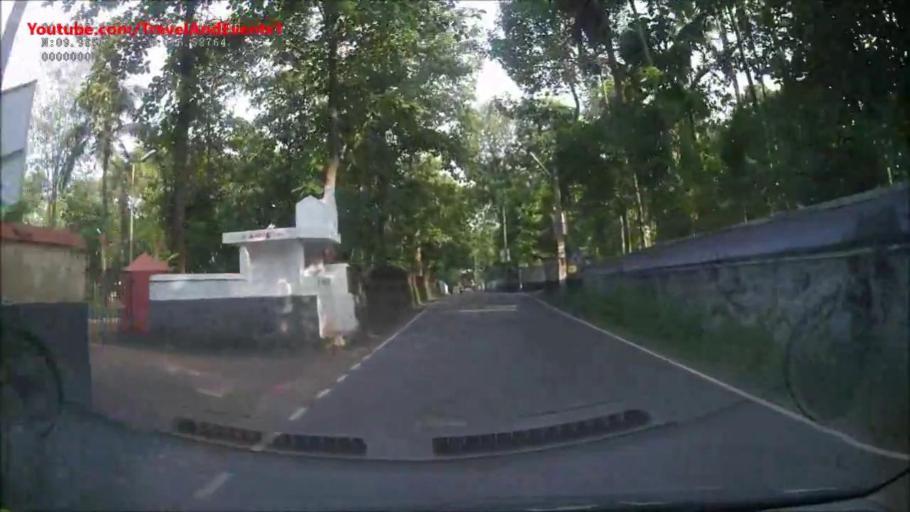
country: IN
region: Kerala
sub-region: Ernakulam
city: Muvattupula
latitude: 9.9833
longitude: 76.5891
